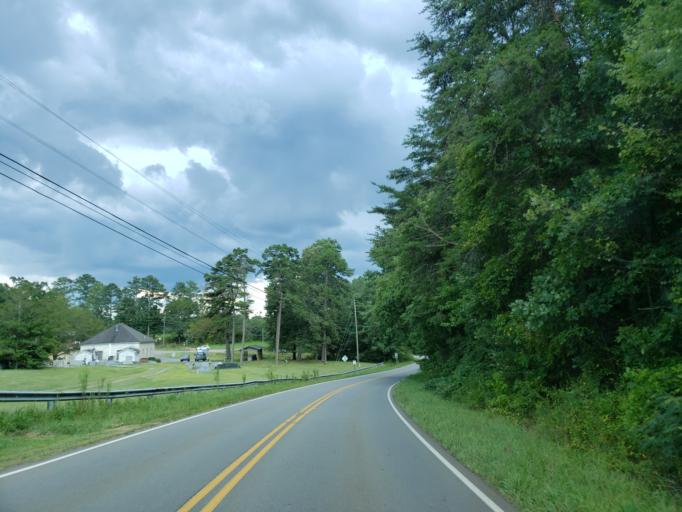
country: US
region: Georgia
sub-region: Pickens County
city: Jasper
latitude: 34.3936
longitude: -84.4675
